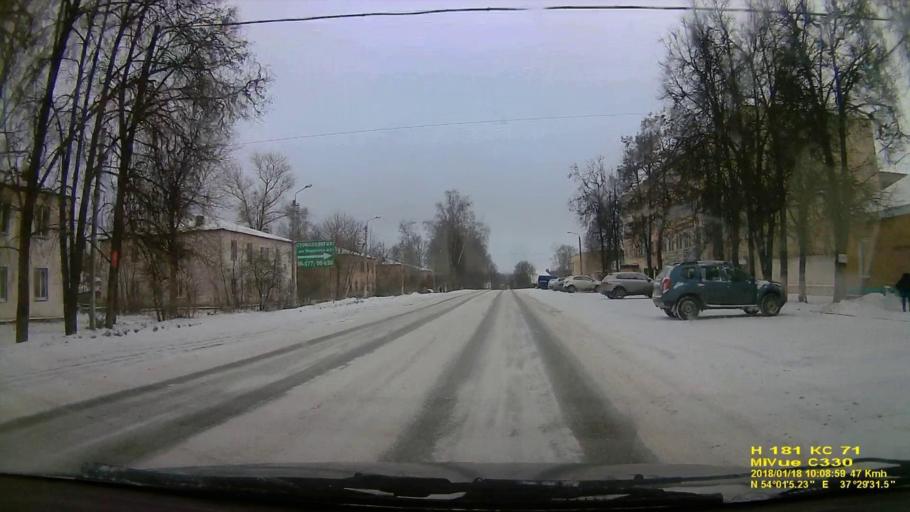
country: RU
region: Tula
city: Pervomayskiy
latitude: 54.0180
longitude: 37.4922
